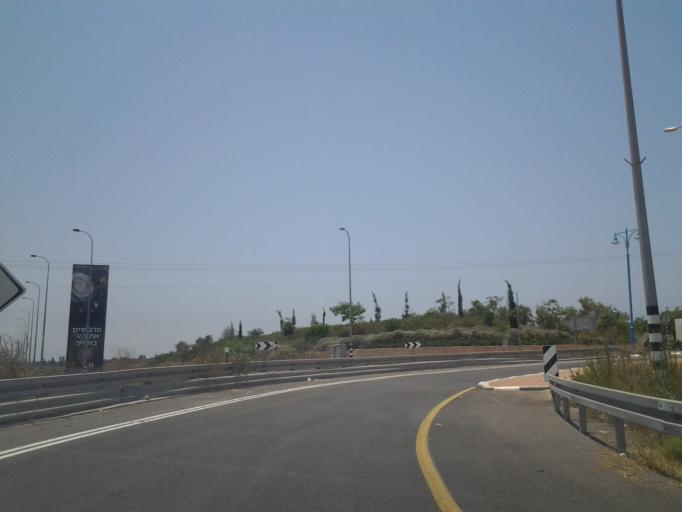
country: IL
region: Haifa
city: Hadera
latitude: 32.4289
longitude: 34.8874
